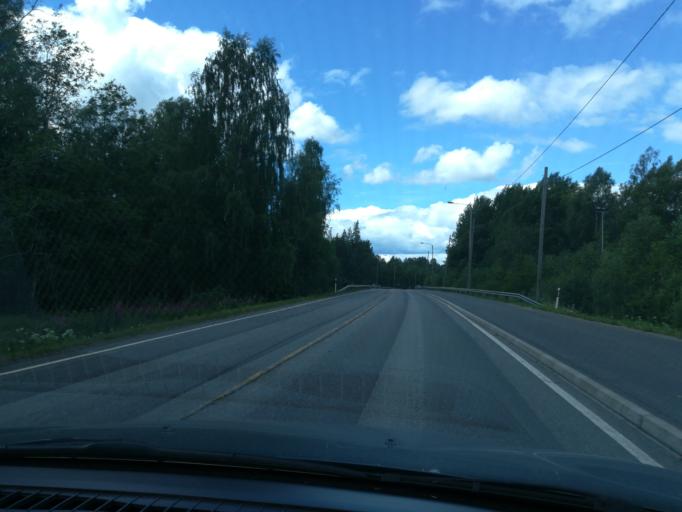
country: FI
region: Southern Savonia
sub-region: Mikkeli
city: Maentyharju
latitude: 61.4349
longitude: 26.8811
